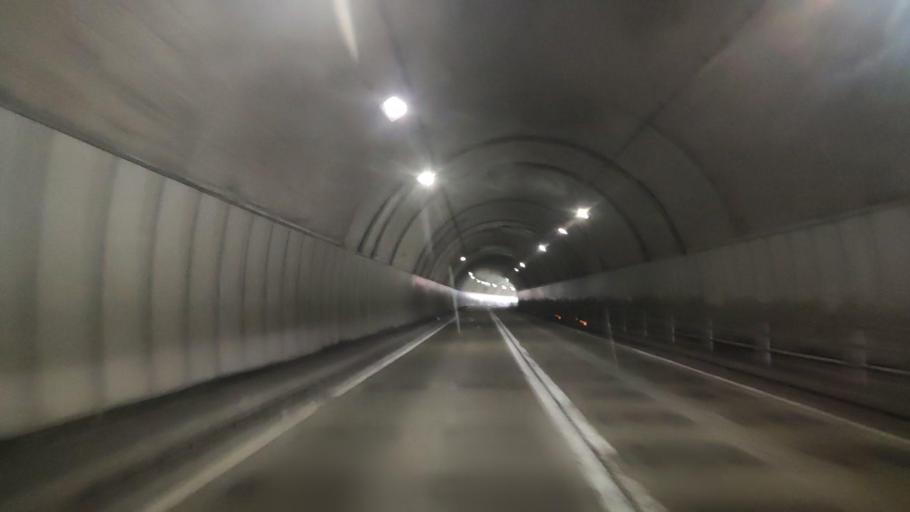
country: JP
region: Shiga Prefecture
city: Nagahama
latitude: 35.4597
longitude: 136.1997
